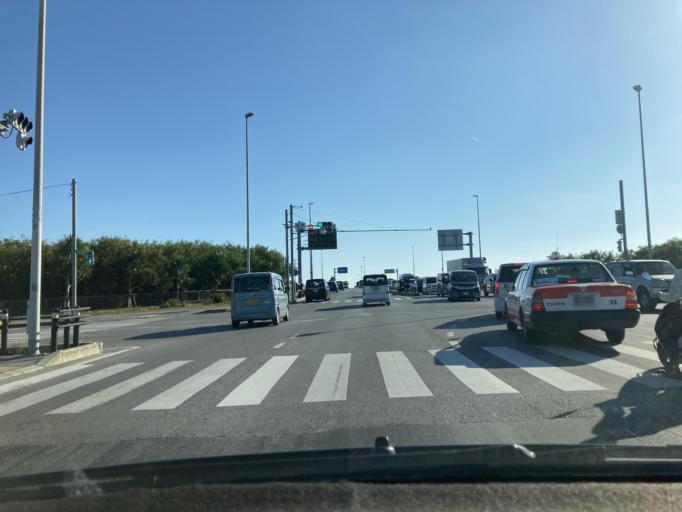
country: JP
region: Okinawa
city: Tomigusuku
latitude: 26.1756
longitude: 127.6531
